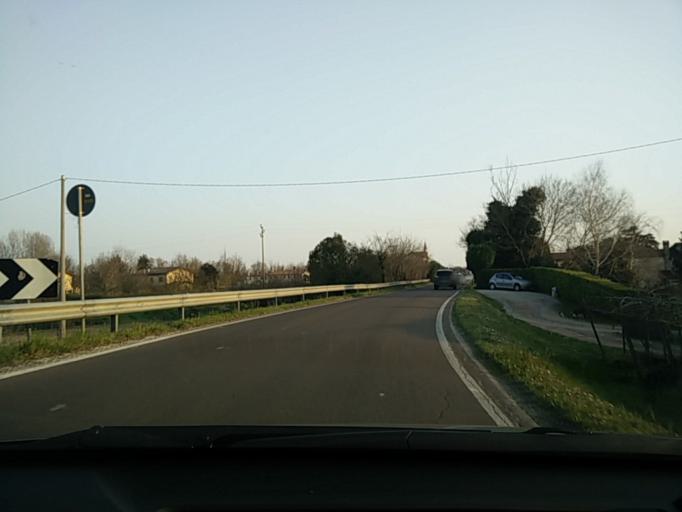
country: IT
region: Veneto
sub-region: Provincia di Venezia
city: Fossalta di Piave
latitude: 45.6554
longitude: 12.5111
